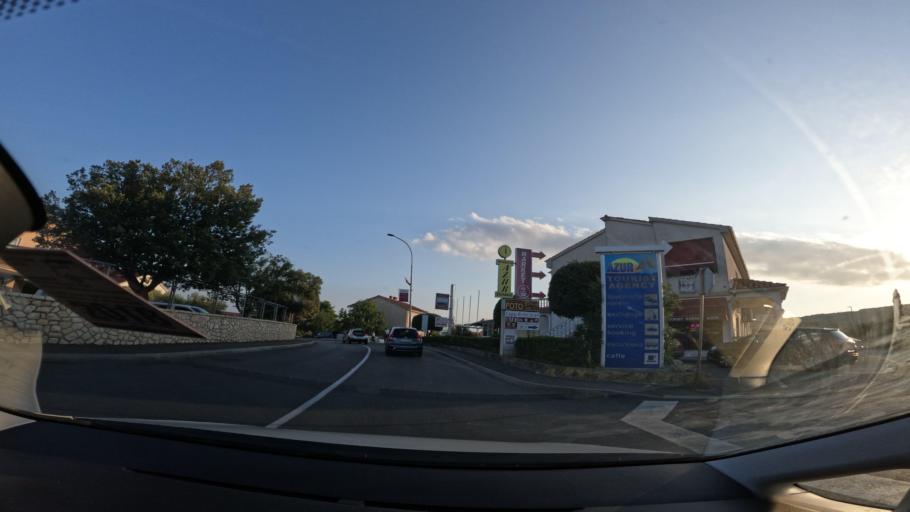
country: HR
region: Primorsko-Goranska
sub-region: Grad Krk
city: Krk
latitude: 45.0270
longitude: 14.5655
